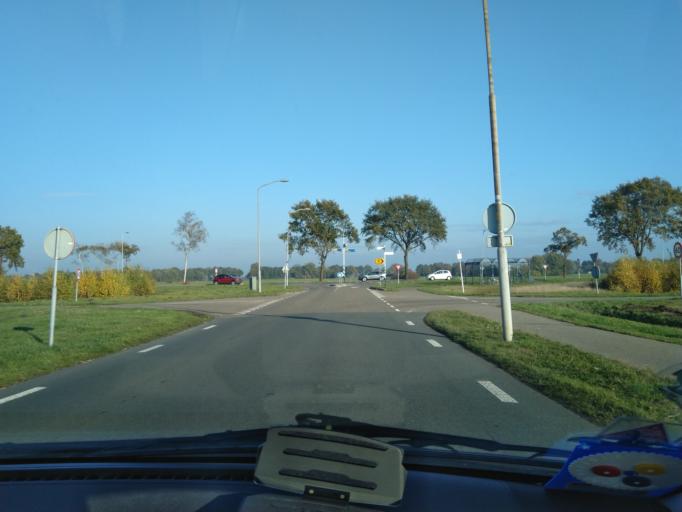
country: NL
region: Groningen
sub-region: Gemeente Hoogezand-Sappemeer
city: Sappemeer
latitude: 53.1255
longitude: 6.7793
